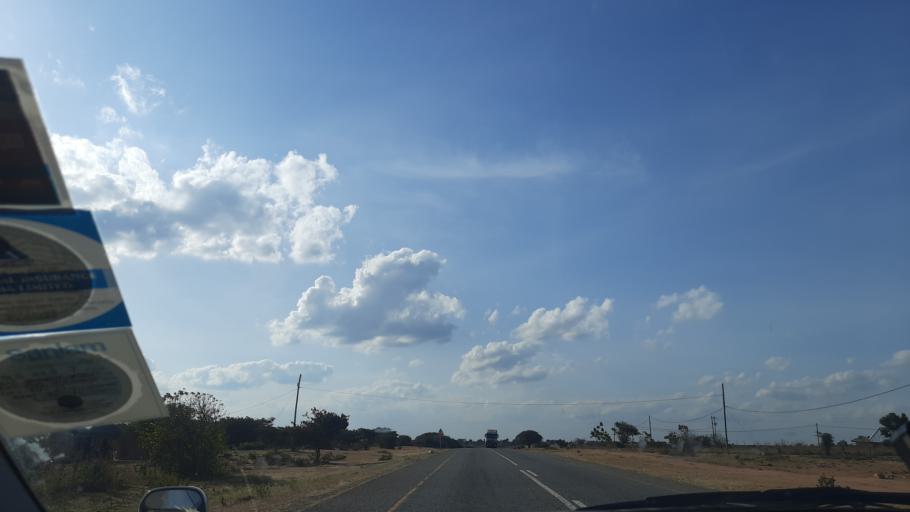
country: TZ
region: Singida
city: Puma
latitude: -4.9478
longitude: 34.7631
